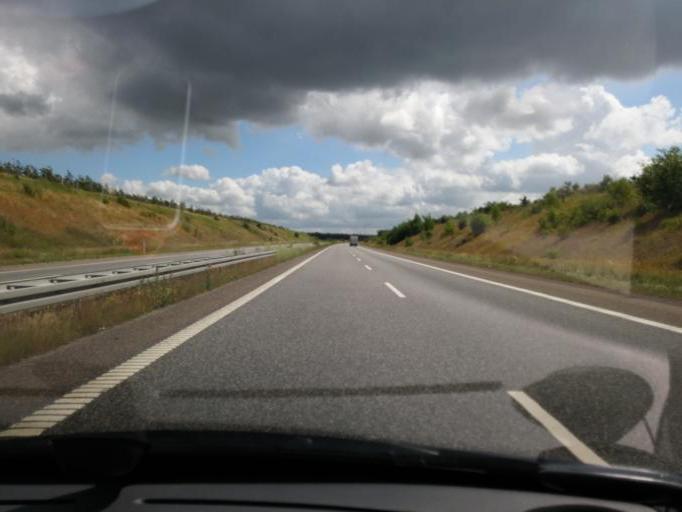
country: DK
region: South Denmark
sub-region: Faaborg-Midtfyn Kommune
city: Arslev
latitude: 55.2852
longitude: 10.4492
